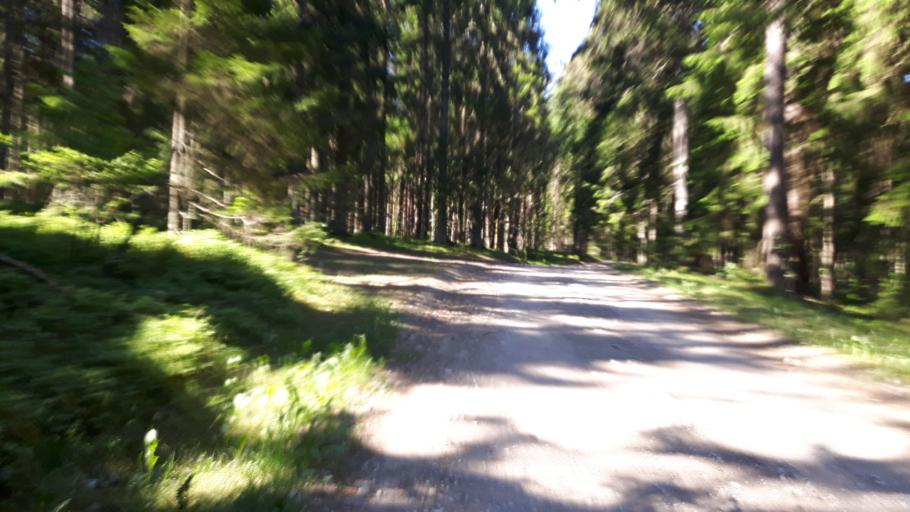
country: EE
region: Harju
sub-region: Loksa linn
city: Loksa
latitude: 59.5600
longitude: 25.8181
